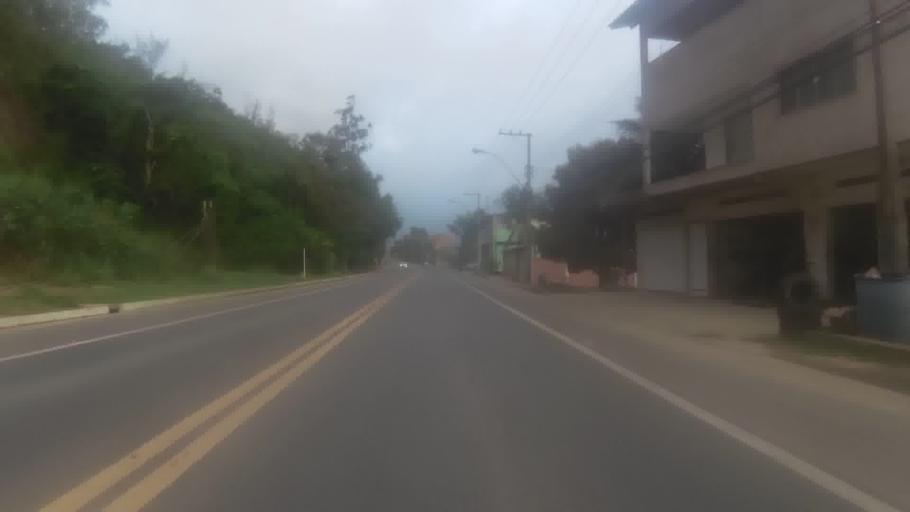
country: BR
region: Espirito Santo
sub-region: Piuma
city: Piuma
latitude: -20.8160
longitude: -40.6297
